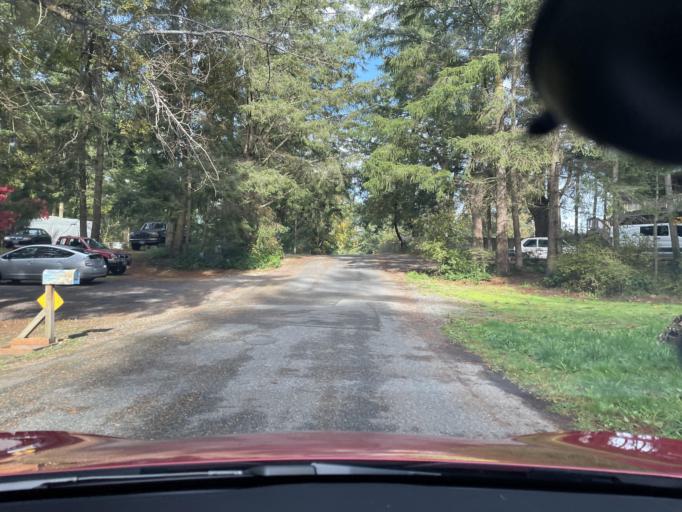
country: US
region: Washington
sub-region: San Juan County
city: Friday Harbor
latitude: 48.5335
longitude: -123.0294
